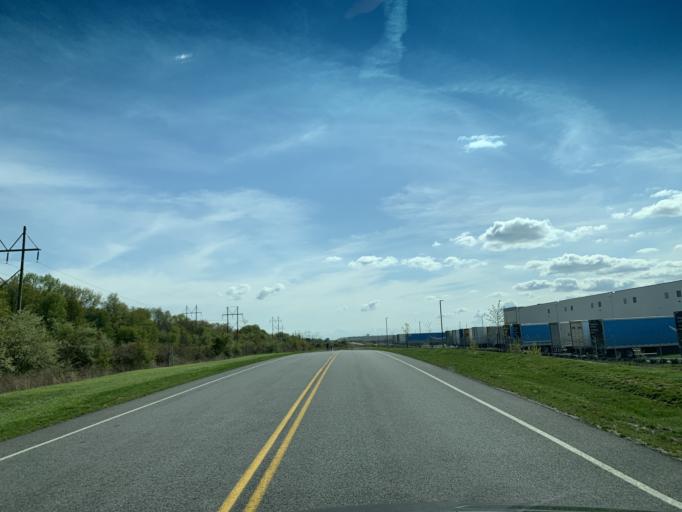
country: US
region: Maryland
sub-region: Harford County
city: Perryman
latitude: 39.4802
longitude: -76.1811
